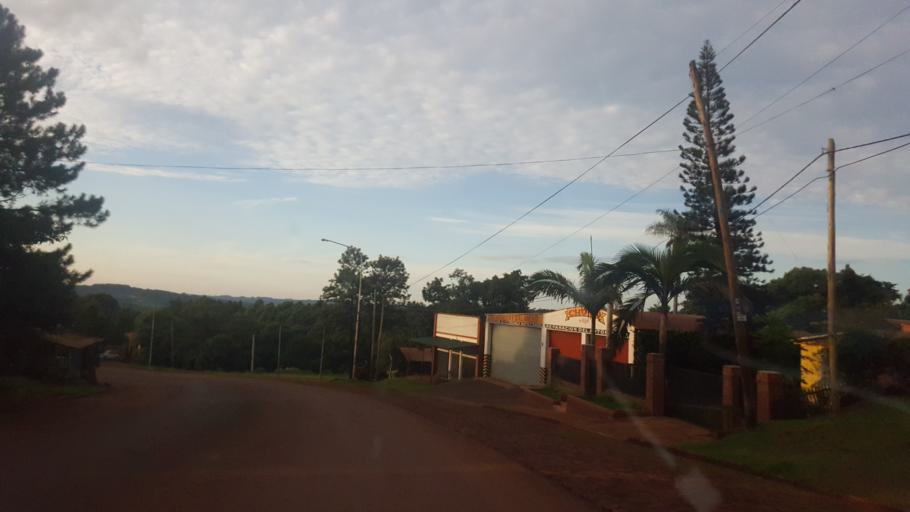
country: AR
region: Misiones
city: Dos de Mayo
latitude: -27.0270
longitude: -54.6880
